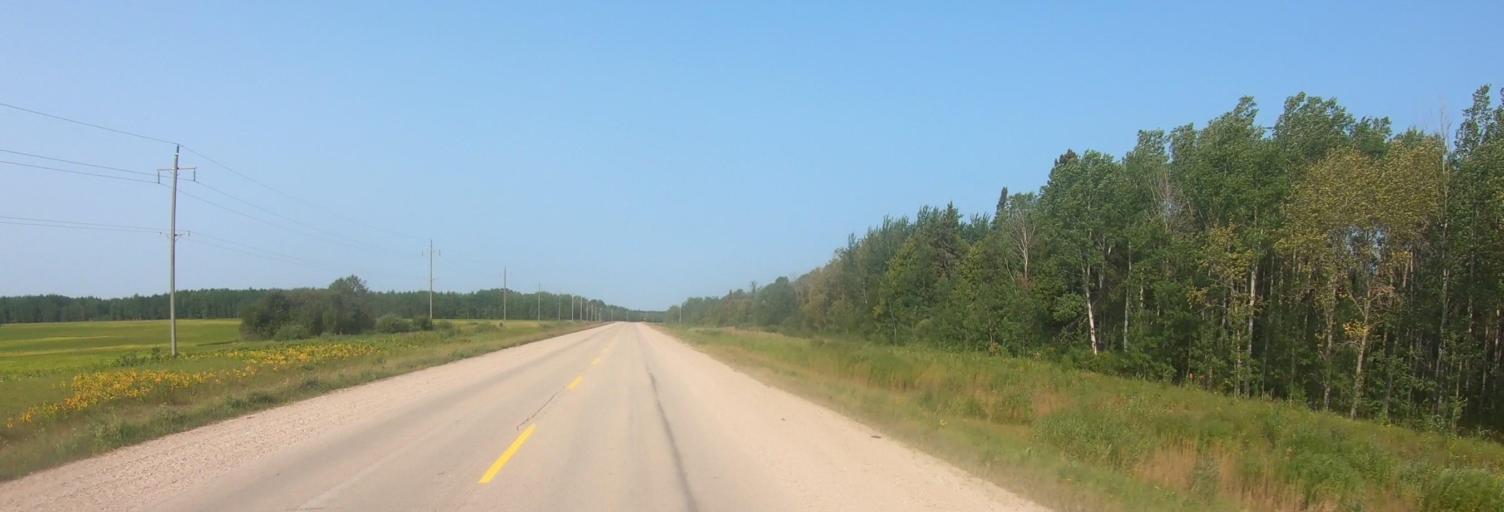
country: US
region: Minnesota
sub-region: Roseau County
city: Roseau
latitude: 49.0234
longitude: -95.7262
